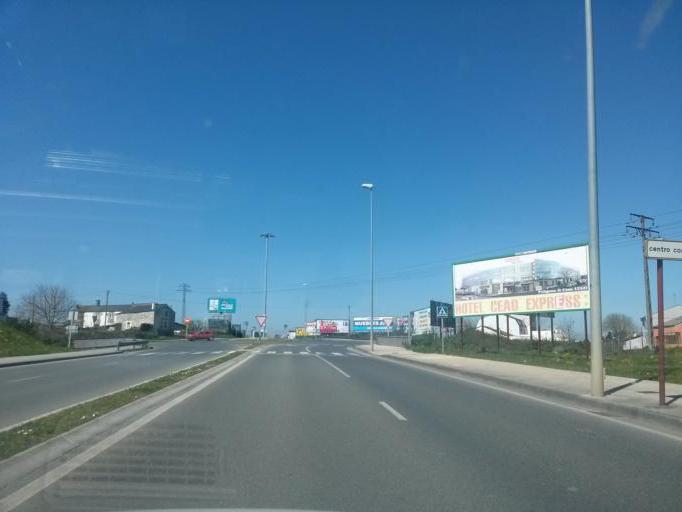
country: ES
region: Galicia
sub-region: Provincia de Lugo
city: Lugo
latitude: 43.0315
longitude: -7.5629
